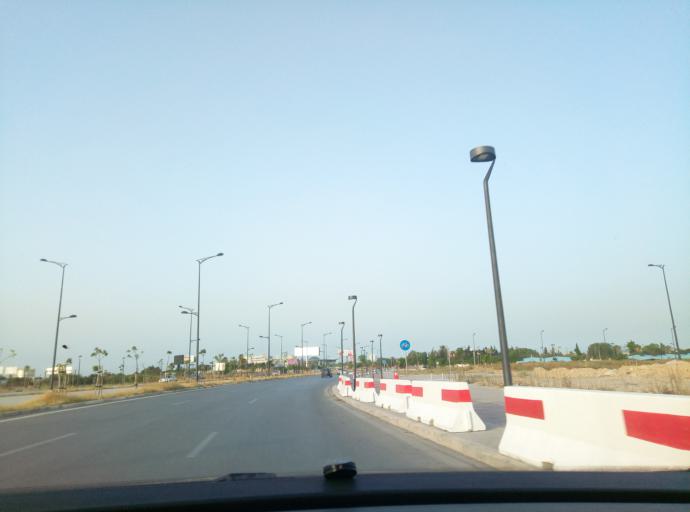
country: TN
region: Ariana
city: Ariana
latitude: 36.8297
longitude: 10.2135
